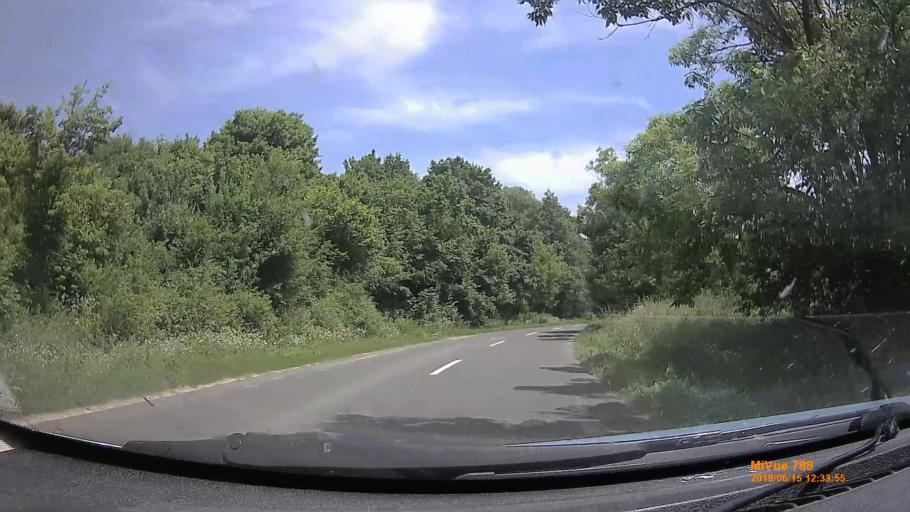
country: HU
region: Baranya
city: Buekkoesd
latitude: 46.1537
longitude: 18.0659
